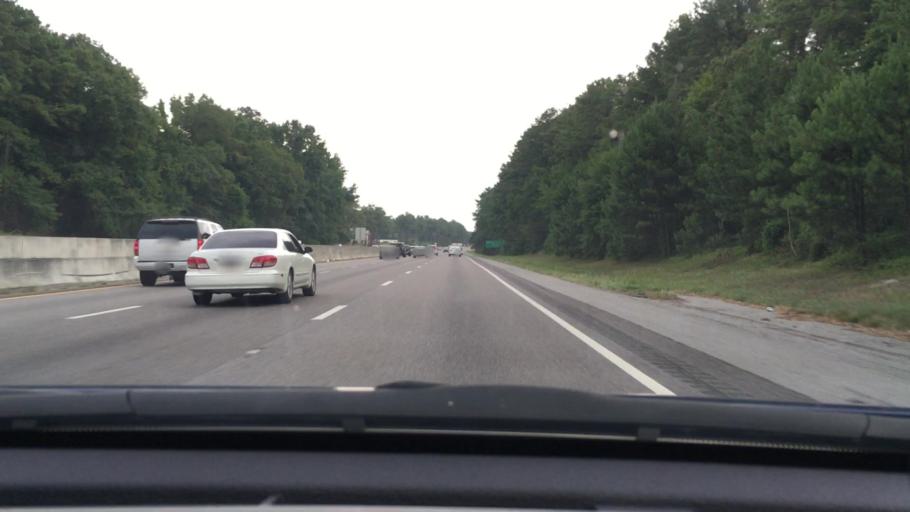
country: US
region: South Carolina
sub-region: Lexington County
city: Springdale
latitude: 33.9648
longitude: -81.0979
